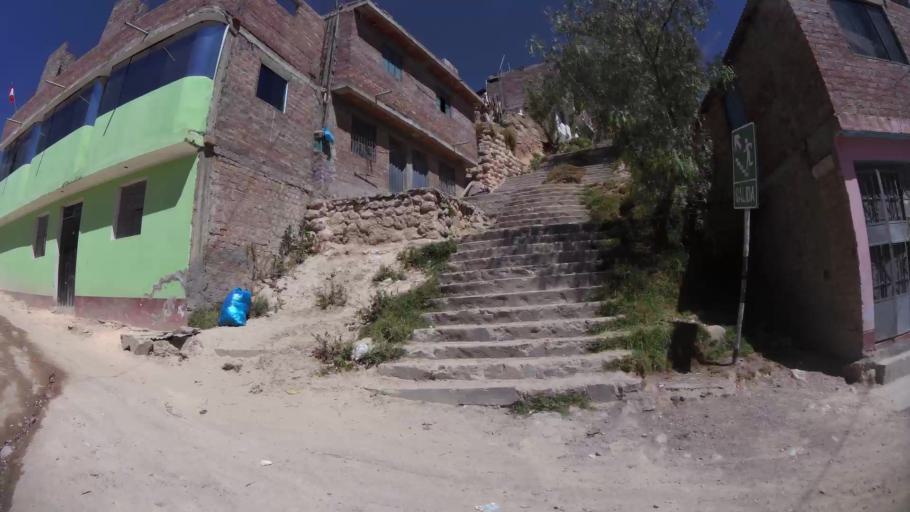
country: PE
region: Ayacucho
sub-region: Provincia de Huamanga
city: Ayacucho
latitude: -13.1656
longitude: -74.2359
